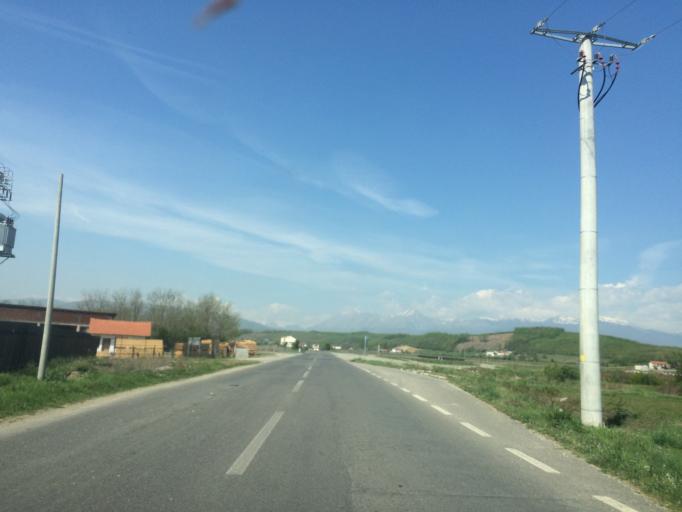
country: XK
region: Gjakova
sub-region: Komuna e Gjakoves
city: Gjakove
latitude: 42.3750
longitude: 20.3975
